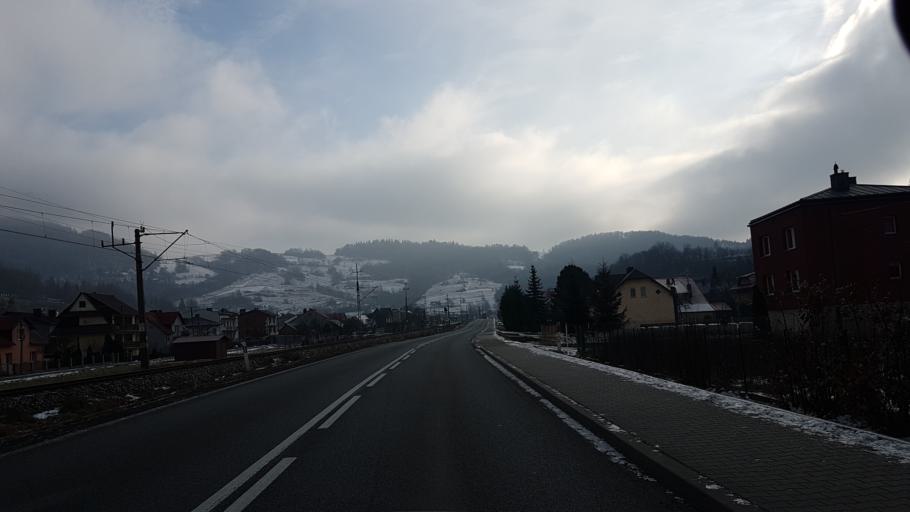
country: PL
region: Lesser Poland Voivodeship
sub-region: Powiat nowosadecki
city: Rytro
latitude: 49.4717
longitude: 20.6905
